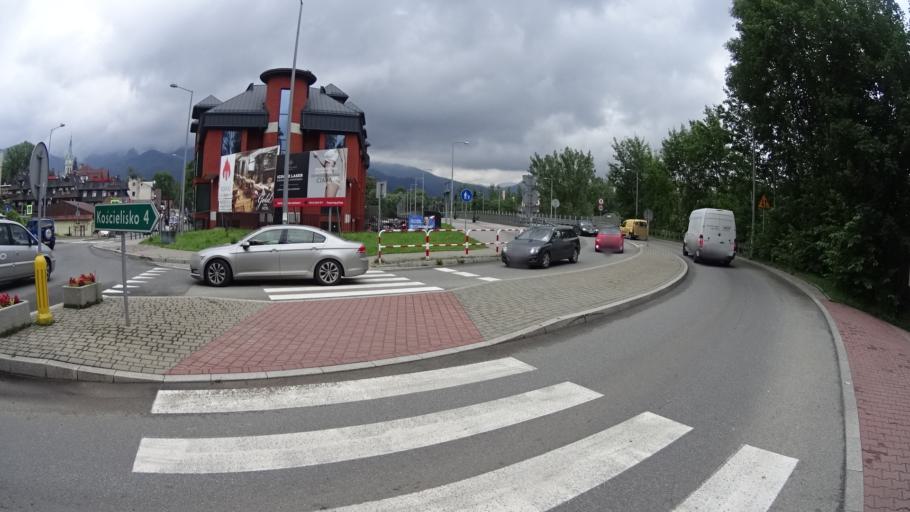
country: PL
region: Lesser Poland Voivodeship
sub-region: Powiat tatrzanski
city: Zakopane
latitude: 49.2992
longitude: 19.9488
